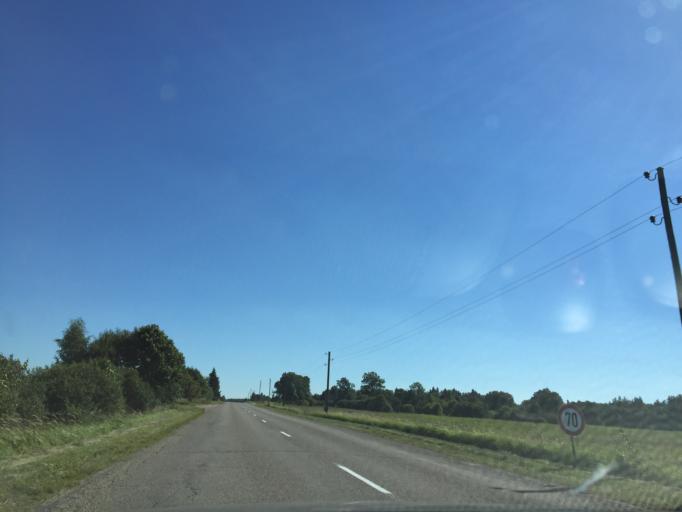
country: LV
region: Akniste
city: Akniste
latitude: 56.1012
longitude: 25.8606
